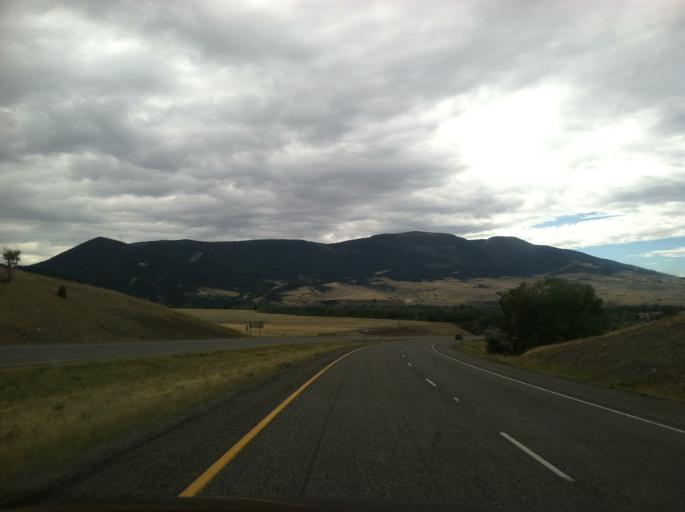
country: US
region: Montana
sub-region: Park County
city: Livingston
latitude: 45.6458
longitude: -110.5517
